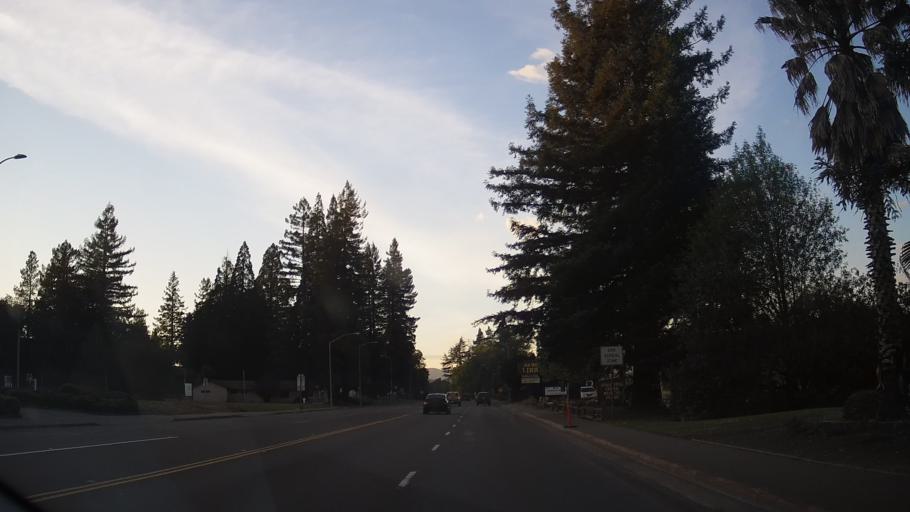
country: US
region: California
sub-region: Mendocino County
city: Willits
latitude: 39.3988
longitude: -123.3495
